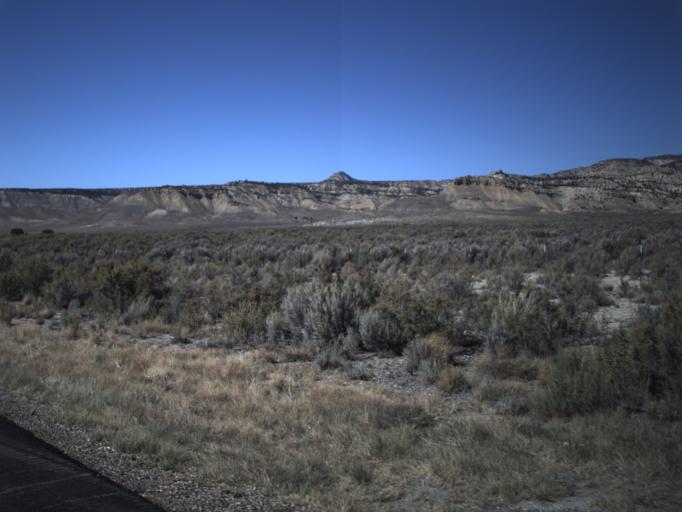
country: US
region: Utah
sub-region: Garfield County
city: Panguitch
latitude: 37.5968
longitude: -111.9473
